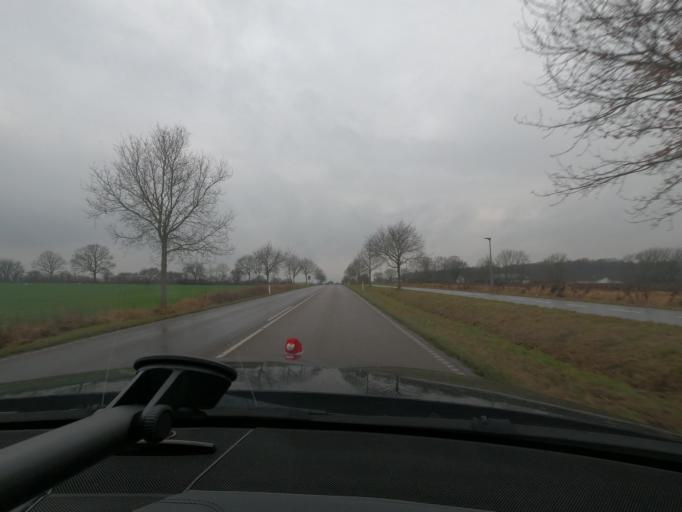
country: DK
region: South Denmark
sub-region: Sonderborg Kommune
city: Horuphav
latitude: 54.9050
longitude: 9.8708
